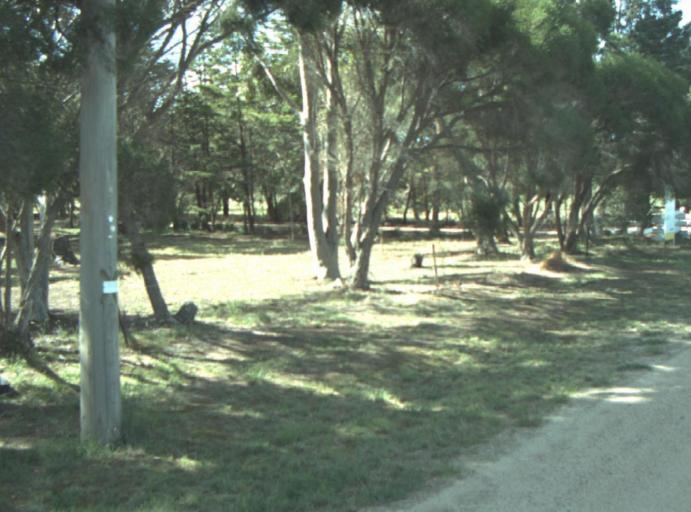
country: AU
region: Victoria
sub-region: Greater Geelong
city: Lara
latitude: -38.0043
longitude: 144.4185
